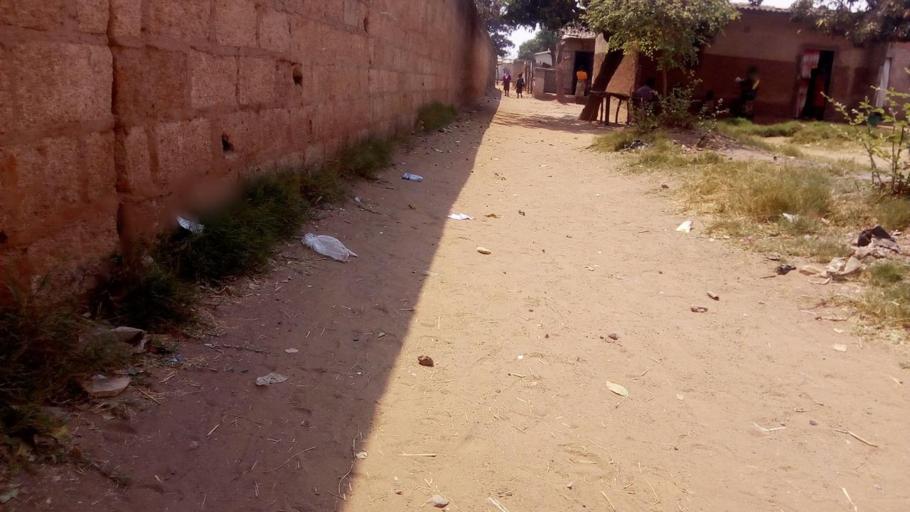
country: ZM
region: Lusaka
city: Lusaka
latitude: -15.3604
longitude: 28.2953
